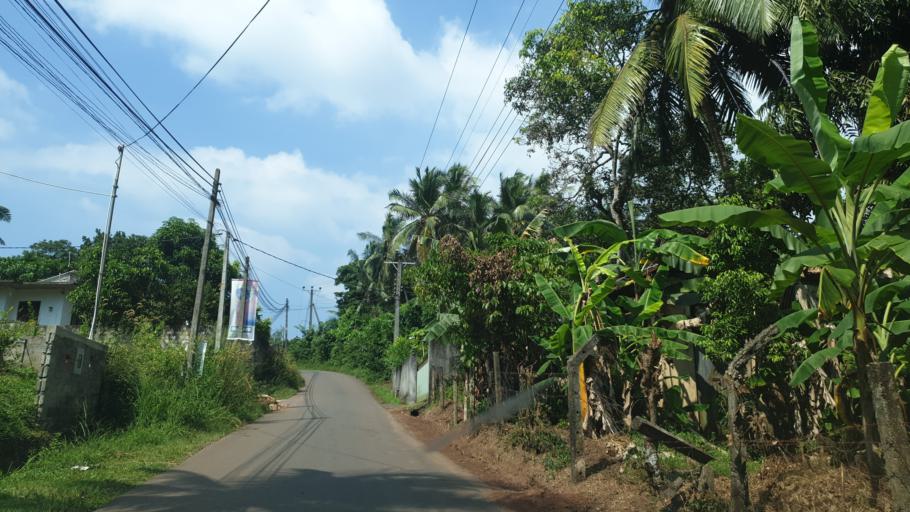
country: LK
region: Western
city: Panadura
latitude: 6.7245
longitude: 79.9542
